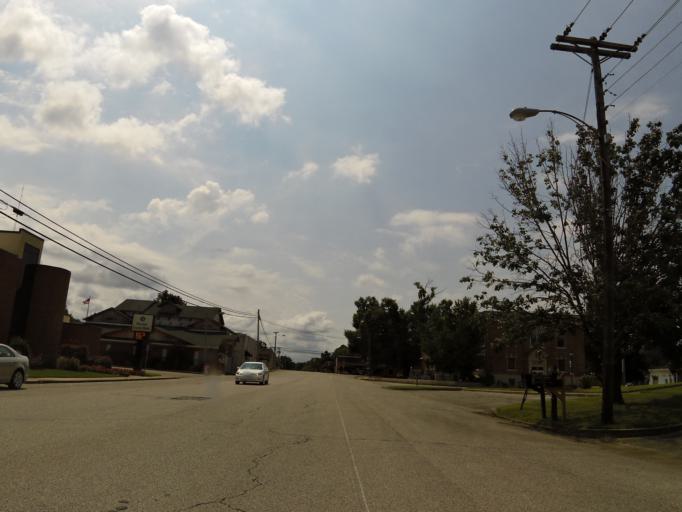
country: US
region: Tennessee
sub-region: Decatur County
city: Decaturville
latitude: 35.5853
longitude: -88.1198
